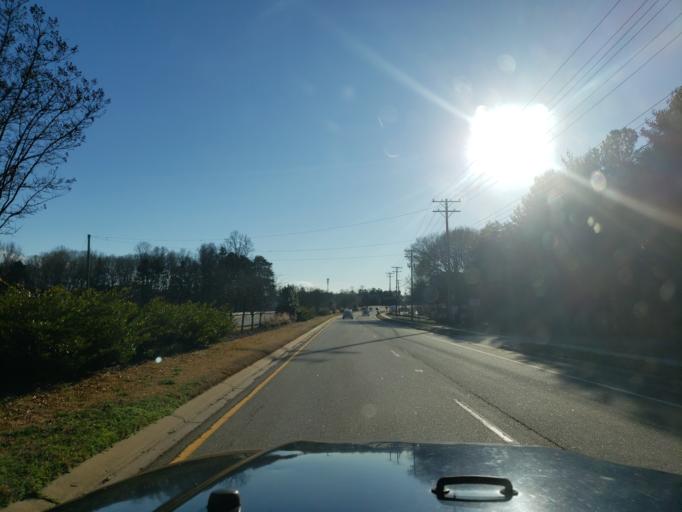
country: US
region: North Carolina
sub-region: Catawba County
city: Lake Norman of Catawba
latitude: 35.5596
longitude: -80.9197
